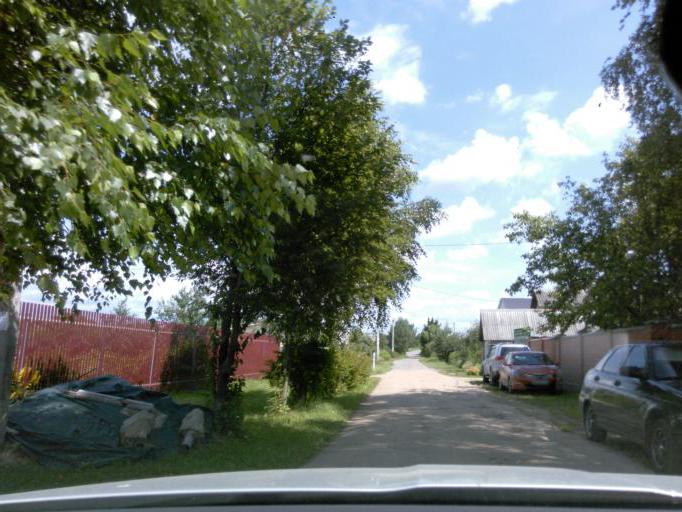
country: RU
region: Moskovskaya
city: Solnechnogorsk
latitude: 56.1299
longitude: 36.9592
